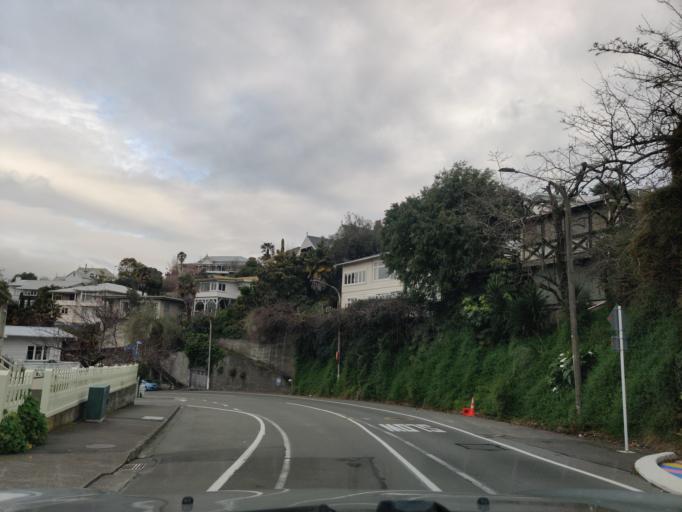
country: NZ
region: Hawke's Bay
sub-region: Napier City
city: Napier
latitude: -39.4860
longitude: 176.9126
